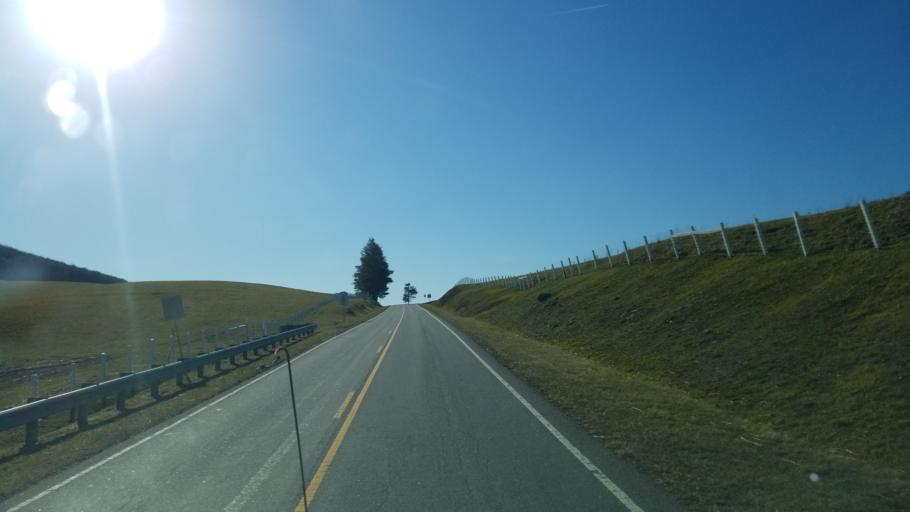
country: US
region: Virginia
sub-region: Giles County
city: Narrows
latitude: 37.1829
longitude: -80.8616
